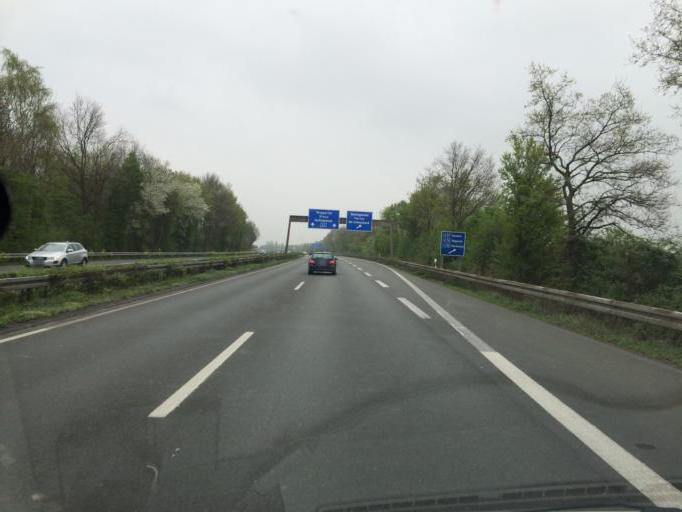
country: DE
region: North Rhine-Westphalia
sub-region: Regierungsbezirk Munster
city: Recklinghausen
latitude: 51.6269
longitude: 7.1663
